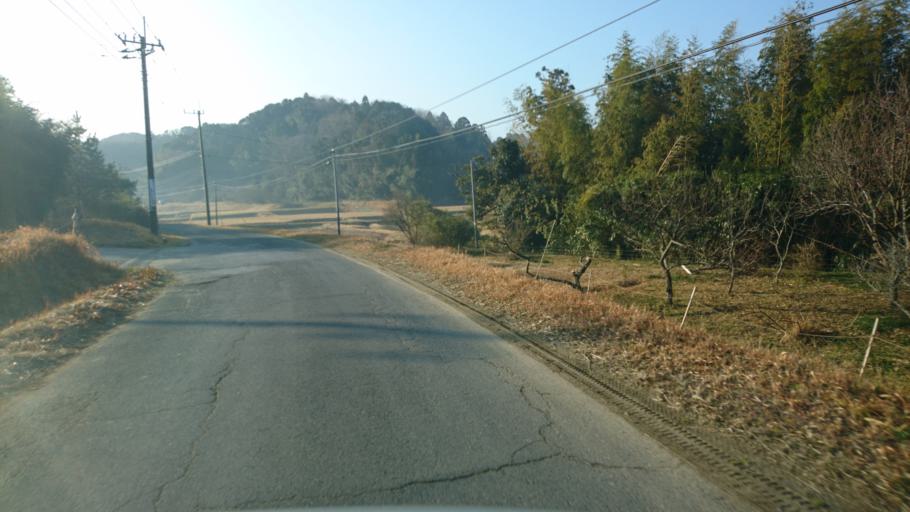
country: JP
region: Chiba
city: Kimitsu
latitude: 35.2950
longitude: 139.9504
